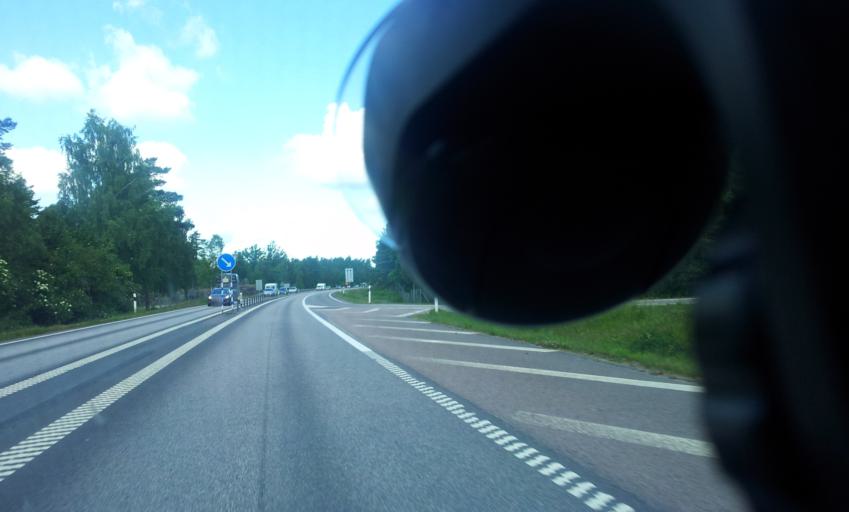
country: SE
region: Kalmar
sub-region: Oskarshamns Kommun
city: Paskallavik
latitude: 57.1277
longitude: 16.4814
